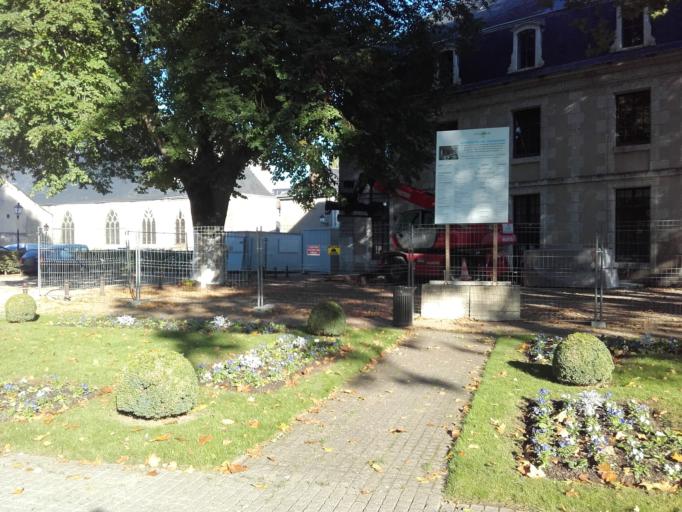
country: FR
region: Centre
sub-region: Departement du Loir-et-Cher
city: Vendome
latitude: 47.7936
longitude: 1.0664
